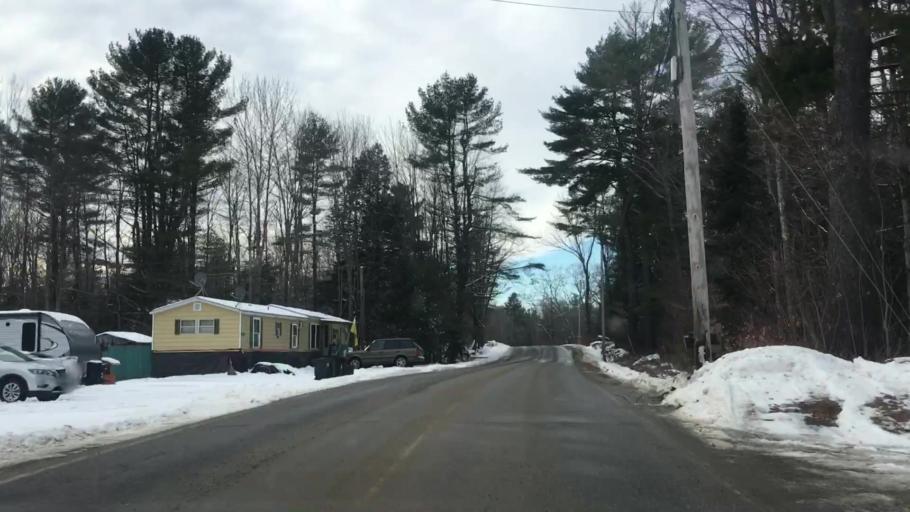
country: US
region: Maine
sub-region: Kennebec County
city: Chelsea
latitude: 44.2511
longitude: -69.7214
